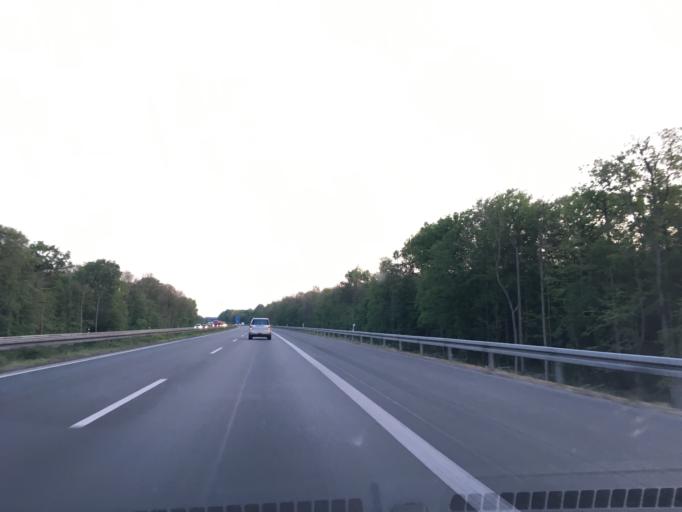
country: DE
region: North Rhine-Westphalia
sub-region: Regierungsbezirk Munster
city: Muenster
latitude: 52.0081
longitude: 7.5774
